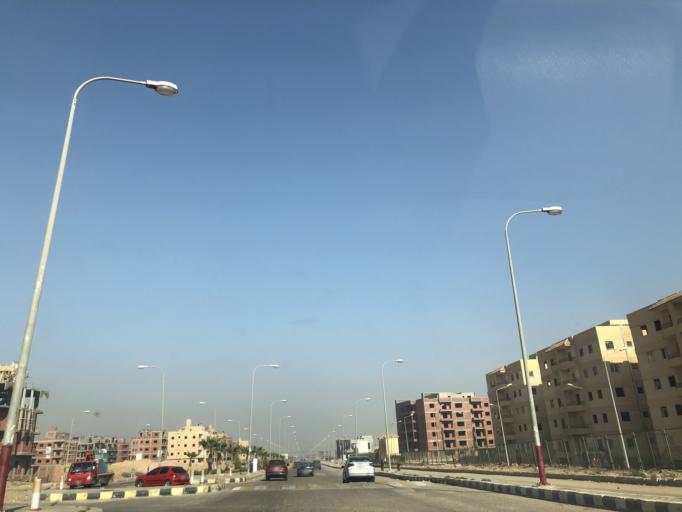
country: EG
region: Al Jizah
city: Madinat Sittah Uktubar
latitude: 29.9367
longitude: 31.0496
